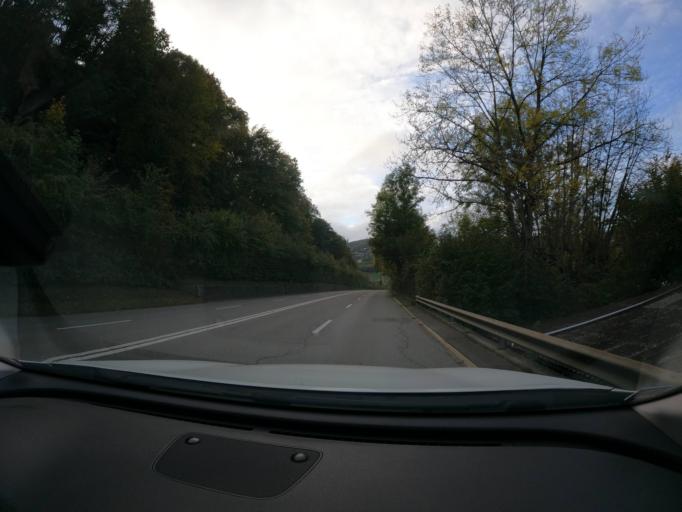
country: CH
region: Bern
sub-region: Bern-Mittelland District
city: Kehrsatz
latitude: 46.9070
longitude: 7.4744
